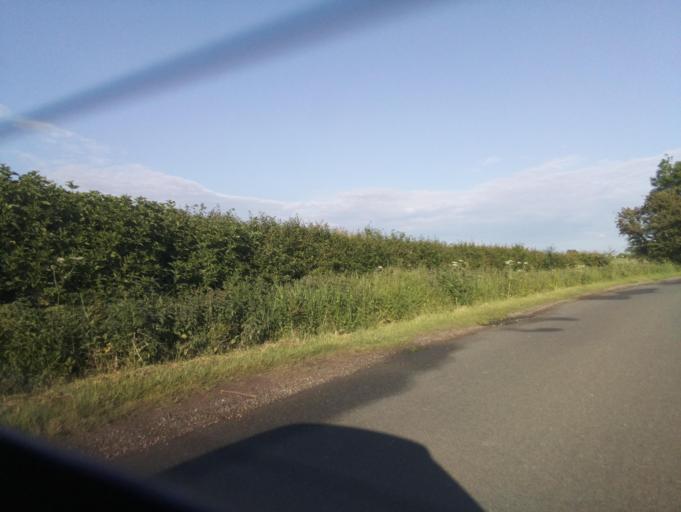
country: GB
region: England
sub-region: Lincolnshire
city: Navenby
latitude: 53.1171
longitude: -0.6231
